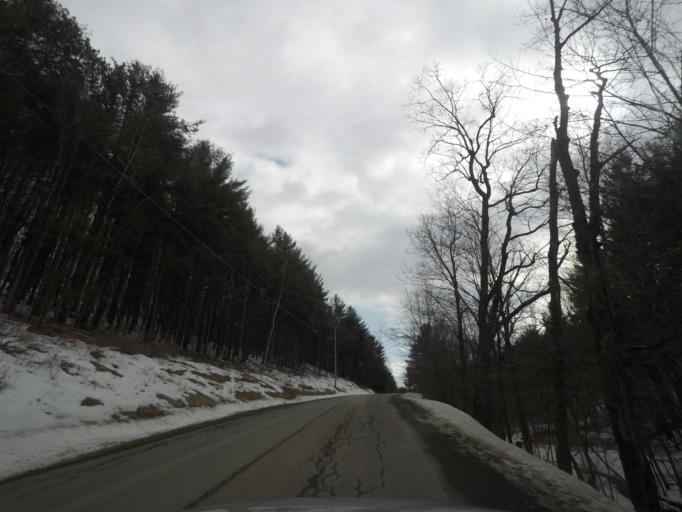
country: US
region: New York
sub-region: Saratoga County
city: Waterford
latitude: 42.7746
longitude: -73.6114
